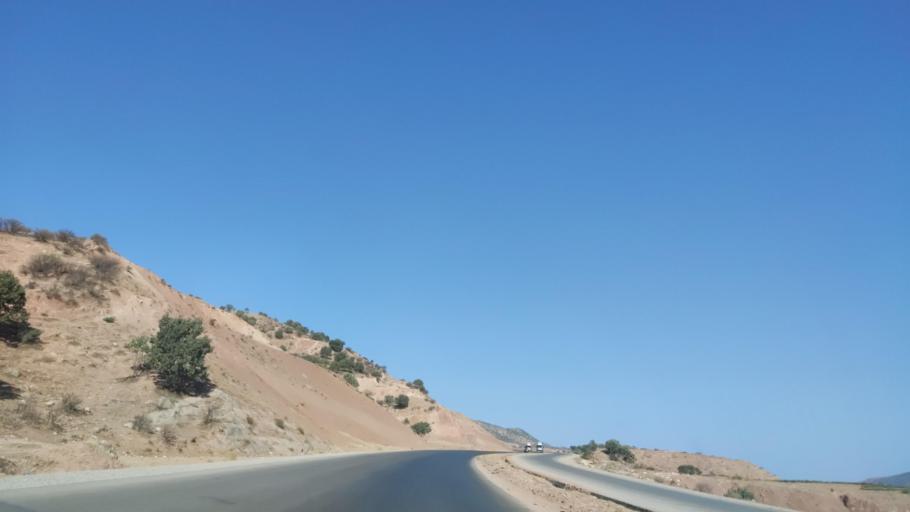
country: IQ
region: Arbil
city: Shaqlawah
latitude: 36.4314
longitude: 44.3143
